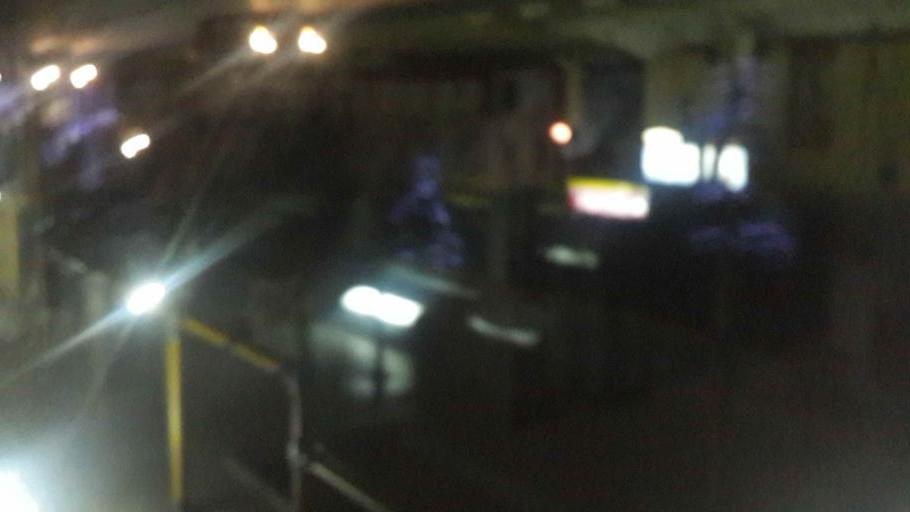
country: RU
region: Tula
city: Tula
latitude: 54.2146
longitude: 37.6232
